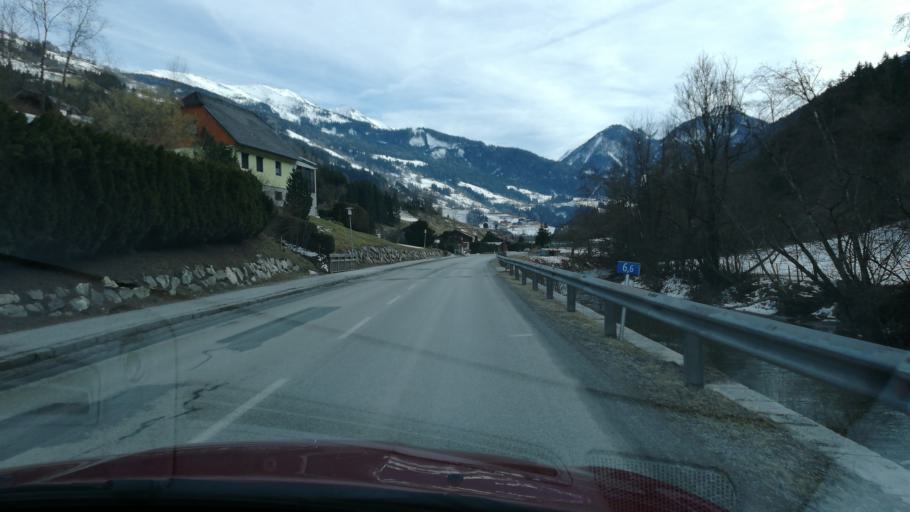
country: AT
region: Styria
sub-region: Politischer Bezirk Liezen
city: Donnersbach
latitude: 47.4744
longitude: 14.1199
